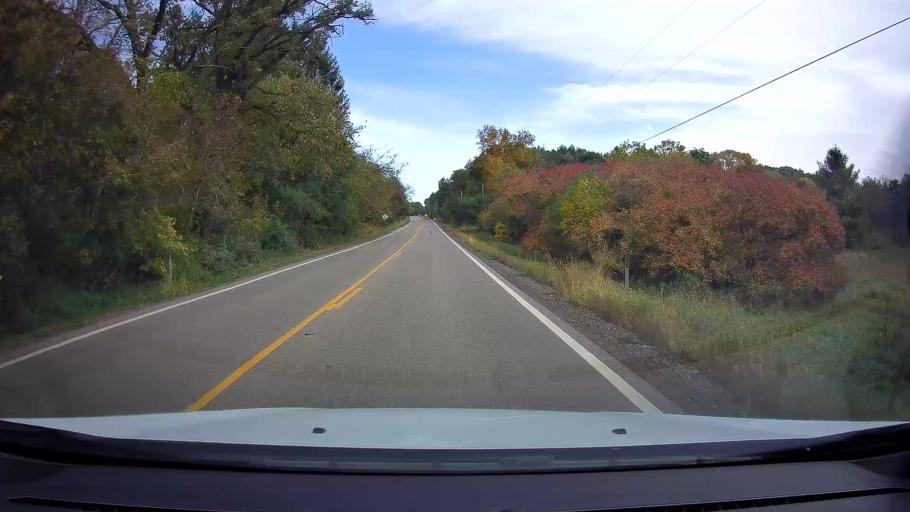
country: US
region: Minnesota
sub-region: Washington County
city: Stillwater
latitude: 45.0832
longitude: -92.8254
